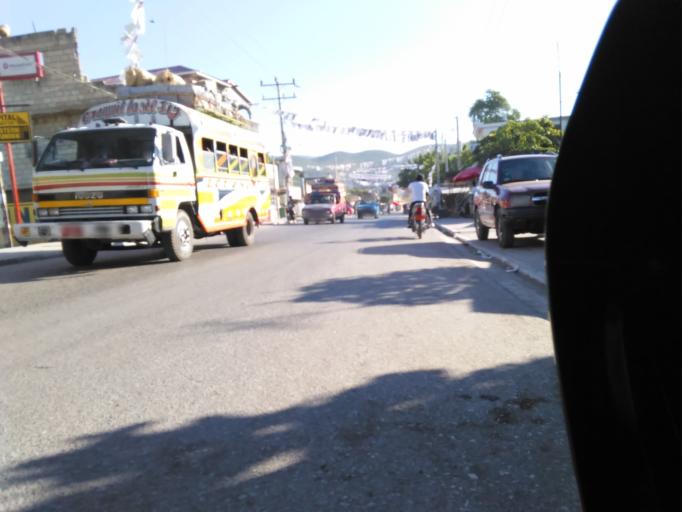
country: HT
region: Artibonite
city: Saint-Marc
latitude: 19.1024
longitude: -72.7016
